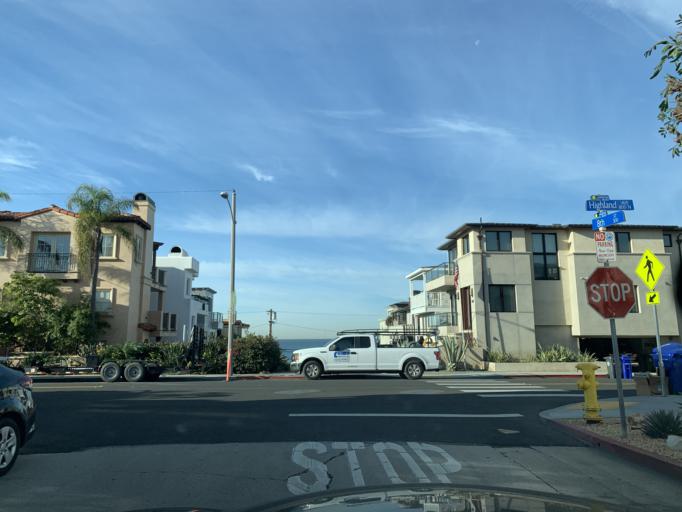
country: US
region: California
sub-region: Los Angeles County
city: Manhattan Beach
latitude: 33.8826
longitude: -118.4081
